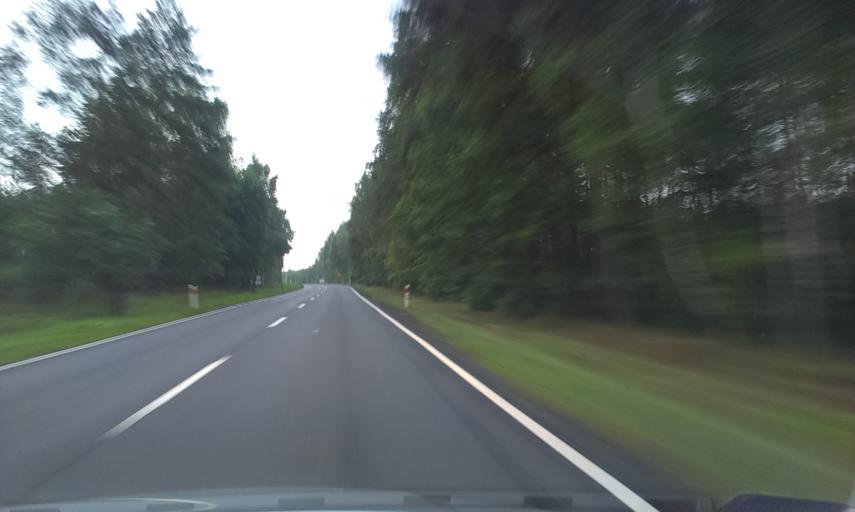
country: PL
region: Greater Poland Voivodeship
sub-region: Powiat zlotowski
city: Tarnowka
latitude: 53.3159
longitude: 16.7945
